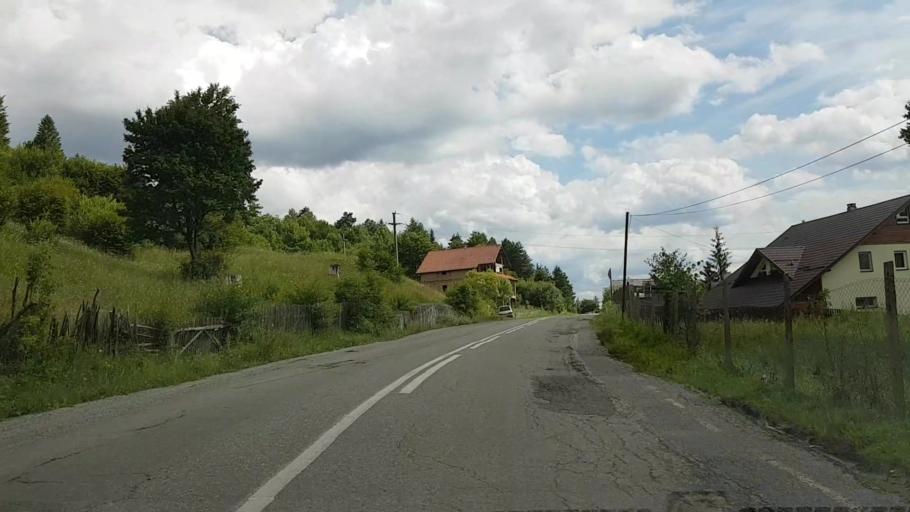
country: RO
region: Neamt
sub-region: Comuna Bicaz
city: Dodeni
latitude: 46.9998
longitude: 26.0985
